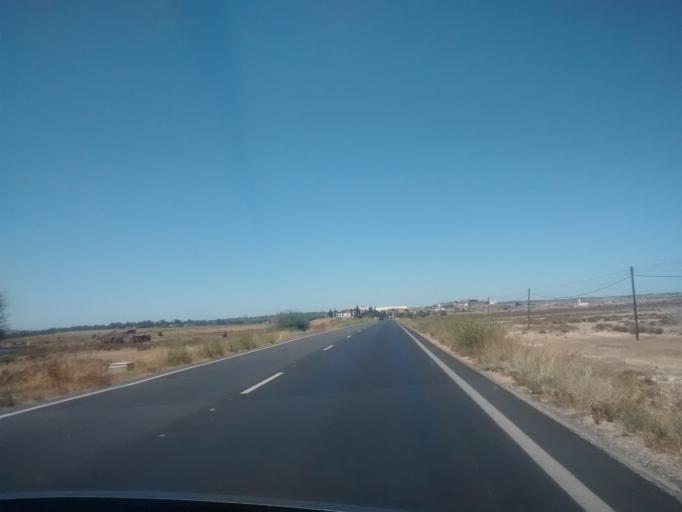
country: PT
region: Faro
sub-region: Vila Real de Santo Antonio
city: Vila Real de Santo Antonio
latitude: 37.2022
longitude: -7.4307
